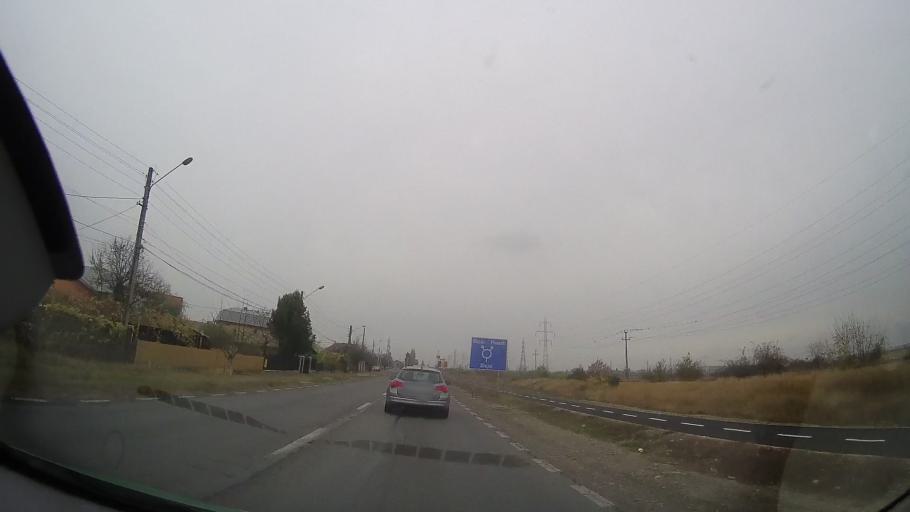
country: RO
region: Prahova
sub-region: Comuna Blejoiu
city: Ploiestiori
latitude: 44.9776
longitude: 26.0172
